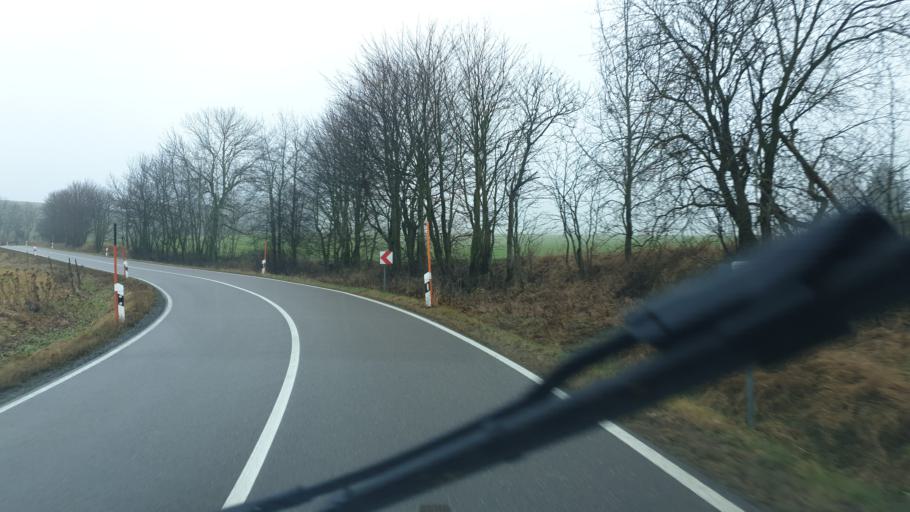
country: DE
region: Saxony
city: Neuhausen
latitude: 50.6645
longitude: 13.4725
